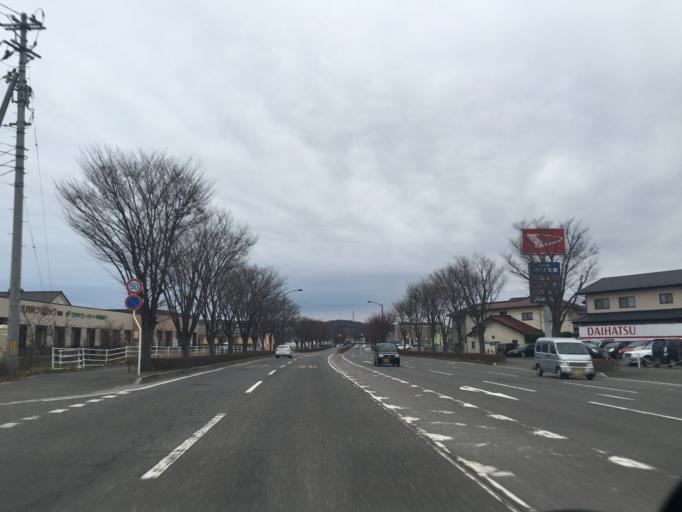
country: JP
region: Fukushima
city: Koriyama
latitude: 37.3978
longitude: 140.4032
